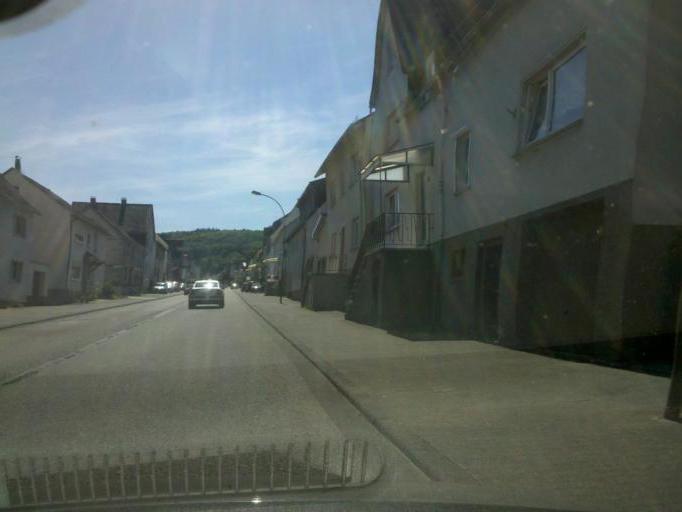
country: DE
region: Hesse
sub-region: Regierungsbezirk Giessen
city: Breitscheid
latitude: 50.7152
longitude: 8.1818
